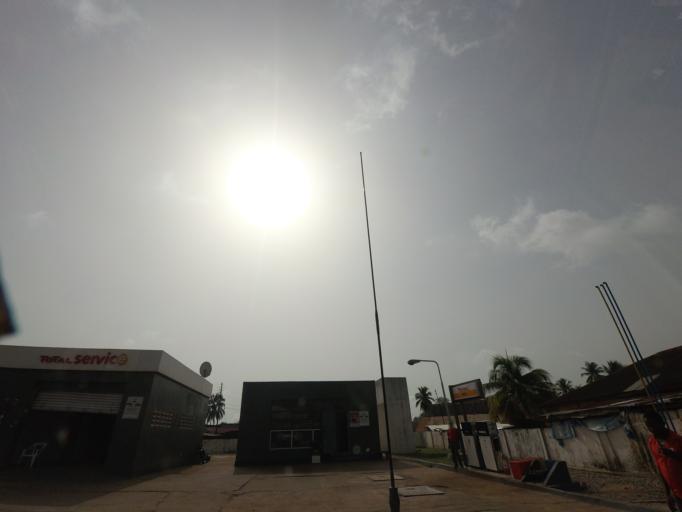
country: SL
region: Southern Province
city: Bo
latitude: 7.9576
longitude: -11.7324
